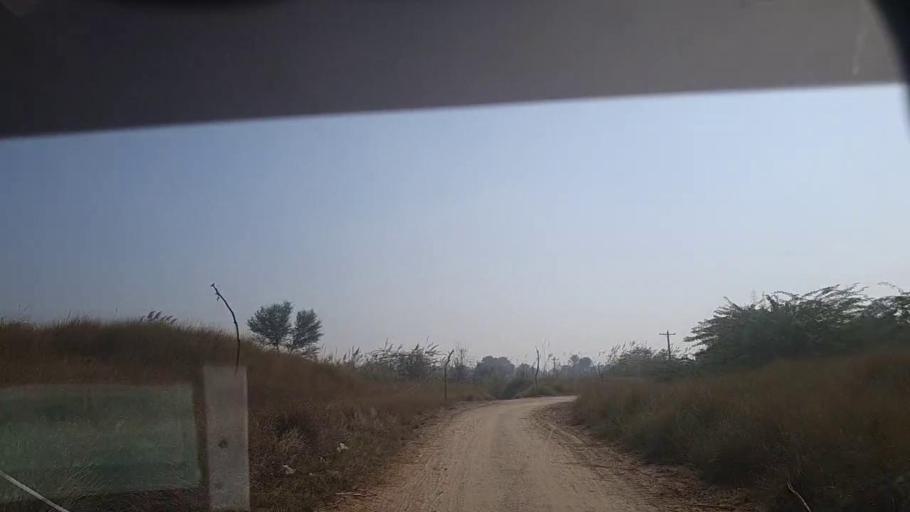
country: PK
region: Sindh
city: Khairpur
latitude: 27.4654
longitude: 68.7398
